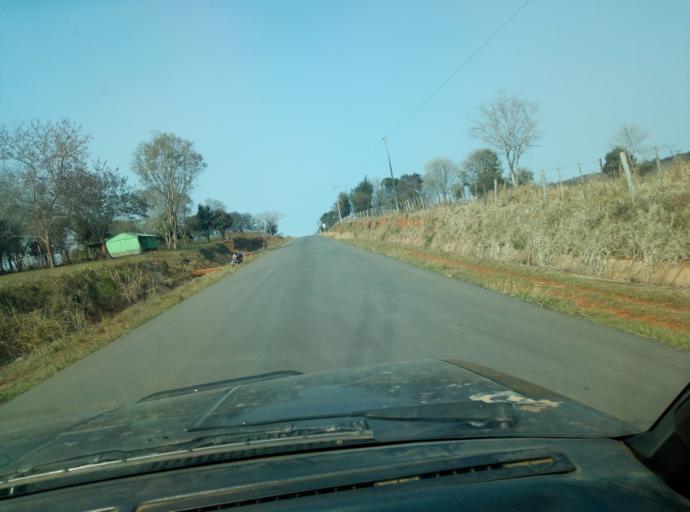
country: PY
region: Caaguazu
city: Carayao
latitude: -25.2604
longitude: -56.2879
